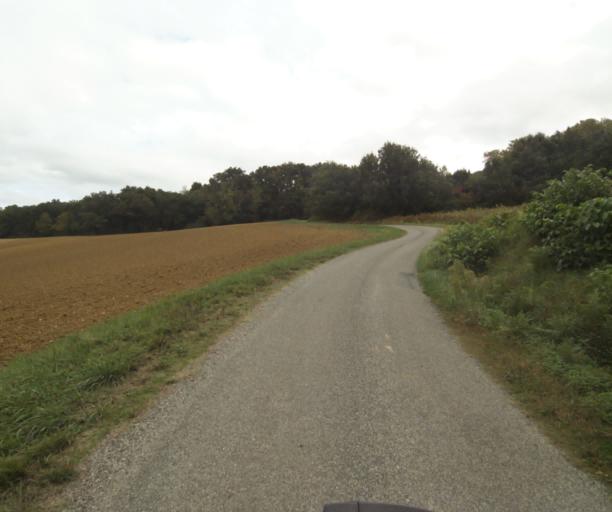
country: FR
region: Midi-Pyrenees
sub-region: Departement du Tarn-et-Garonne
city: Verdun-sur-Garonne
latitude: 43.8453
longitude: 1.1182
